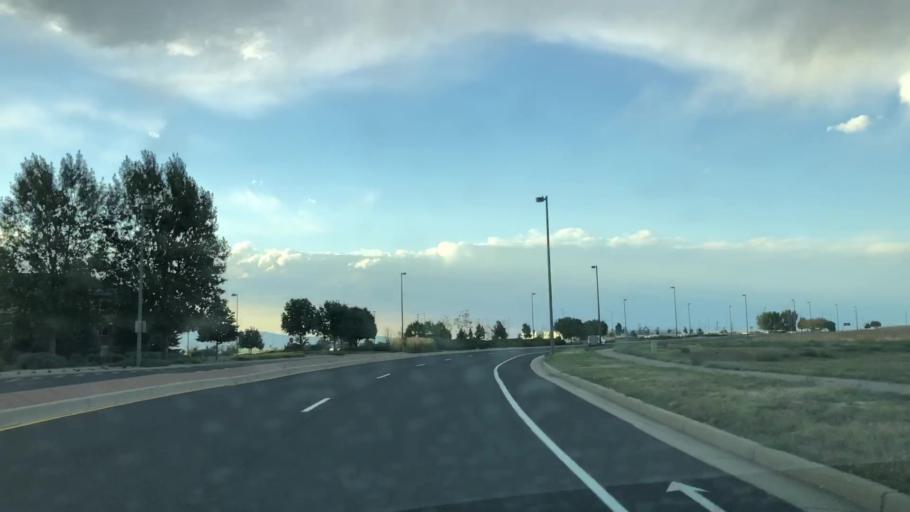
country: US
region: Colorado
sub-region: Larimer County
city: Loveland
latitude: 40.4209
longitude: -104.9975
